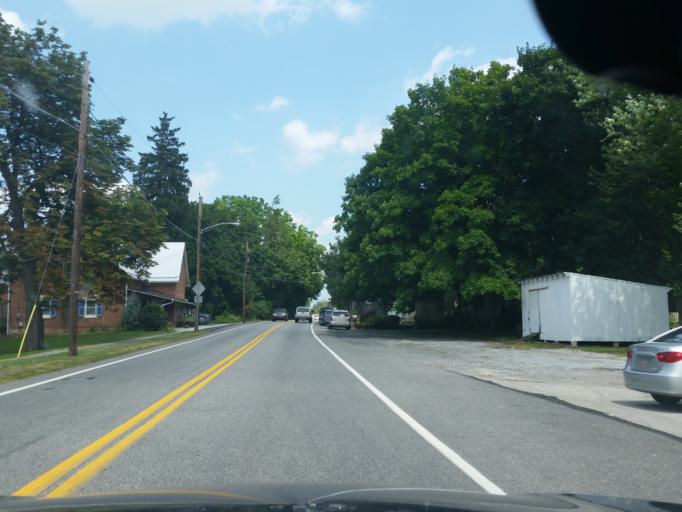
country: US
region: Pennsylvania
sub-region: Cumberland County
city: Boiling Springs
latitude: 40.1654
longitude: -77.0842
